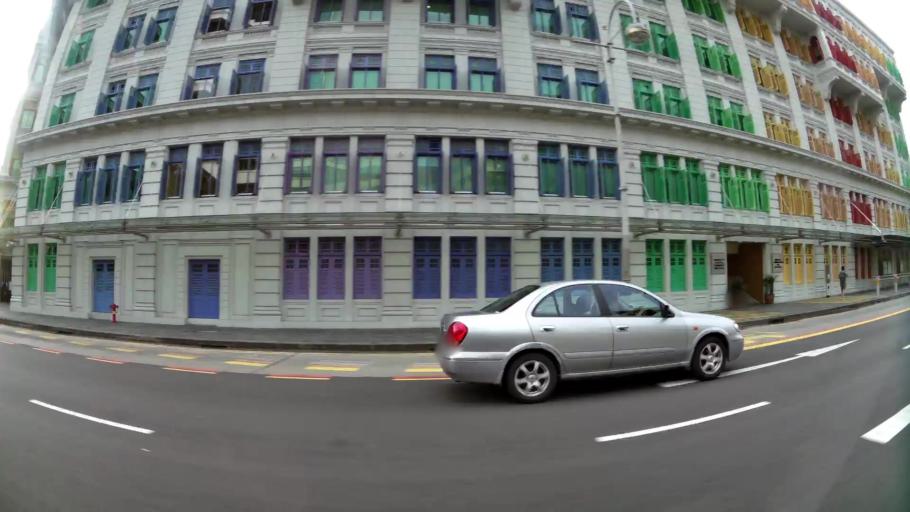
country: SG
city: Singapore
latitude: 1.2905
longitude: 103.8486
